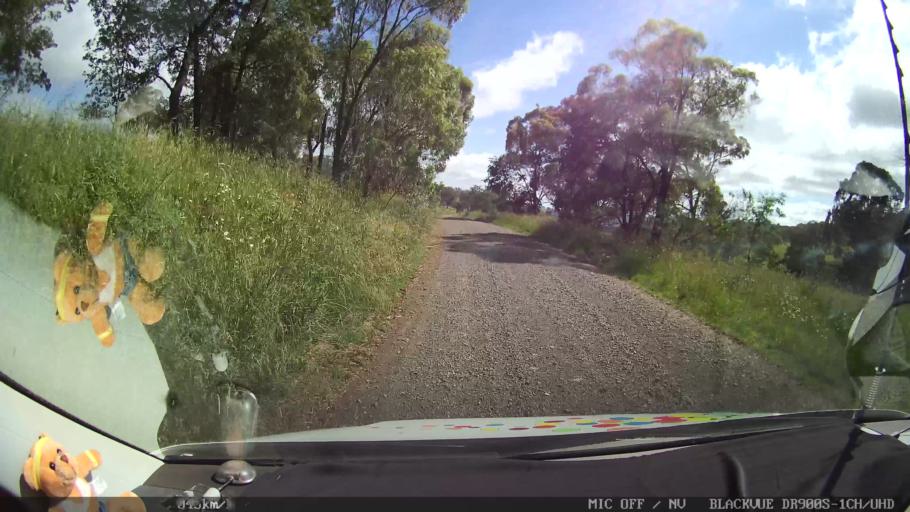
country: AU
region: New South Wales
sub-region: Guyra
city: Guyra
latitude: -30.0043
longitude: 151.6689
